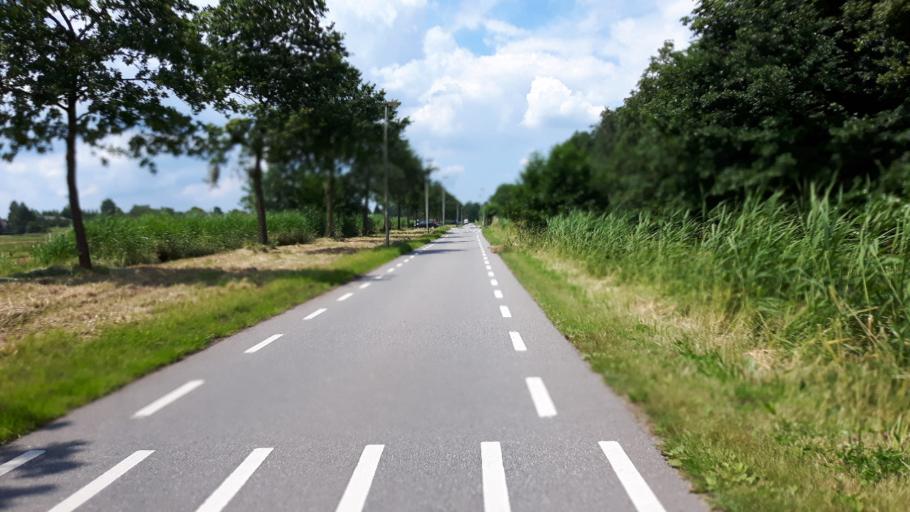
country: NL
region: South Holland
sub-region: Gemeente Boskoop
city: Boskoop
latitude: 52.0829
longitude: 4.6970
